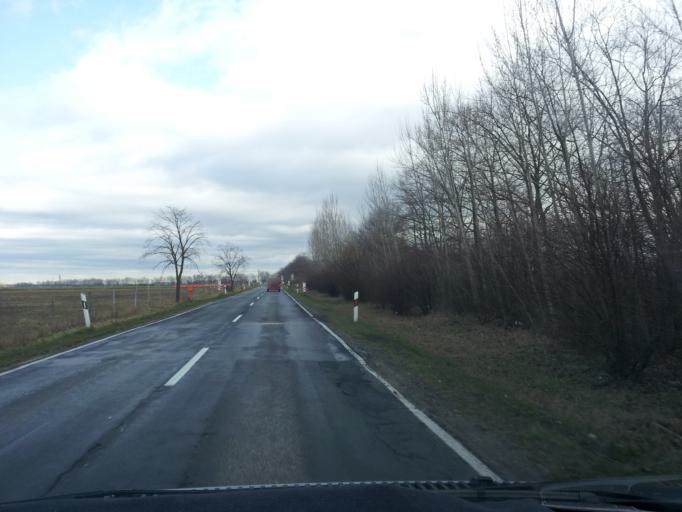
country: HU
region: Vas
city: Gencsapati
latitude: 47.2747
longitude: 16.6089
